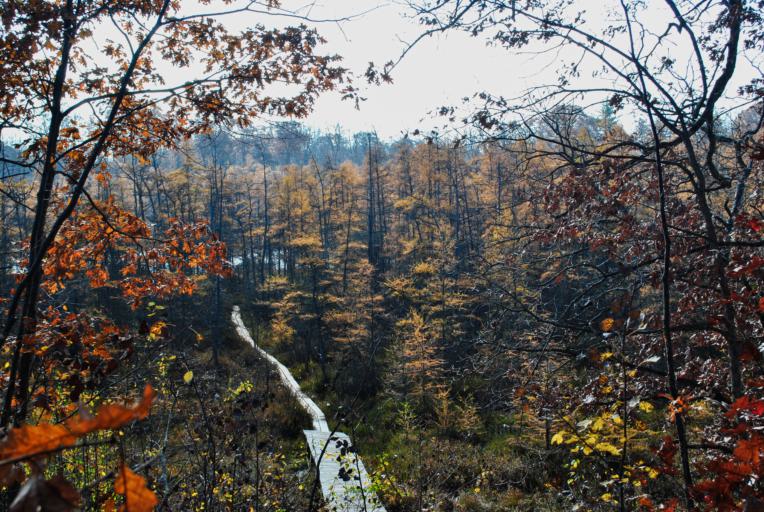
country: US
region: Wisconsin
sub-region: Walworth County
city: East Troy
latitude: 42.8205
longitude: -88.4074
